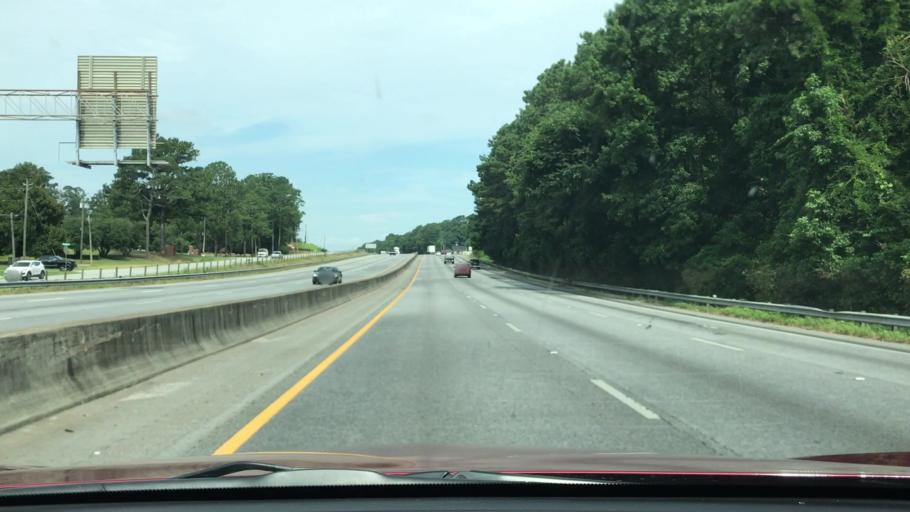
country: US
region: Georgia
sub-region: Newton County
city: Oxford
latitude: 33.6105
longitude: -83.8869
